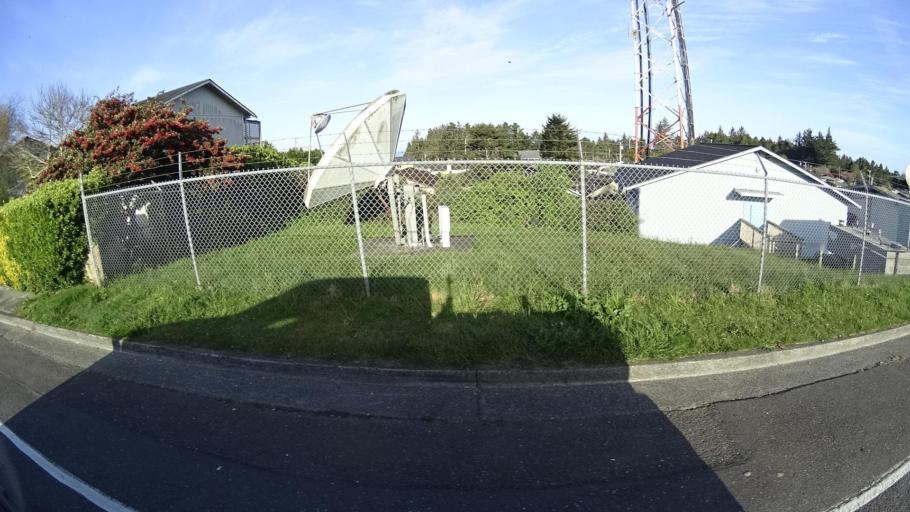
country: US
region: California
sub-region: Humboldt County
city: Humboldt Hill
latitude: 40.7163
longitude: -124.2032
